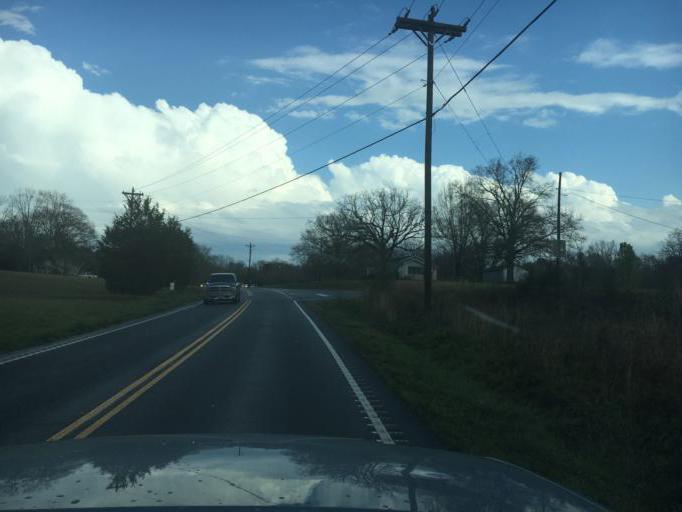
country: US
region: South Carolina
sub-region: Greenville County
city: Parker
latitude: 34.8558
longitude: -82.5006
